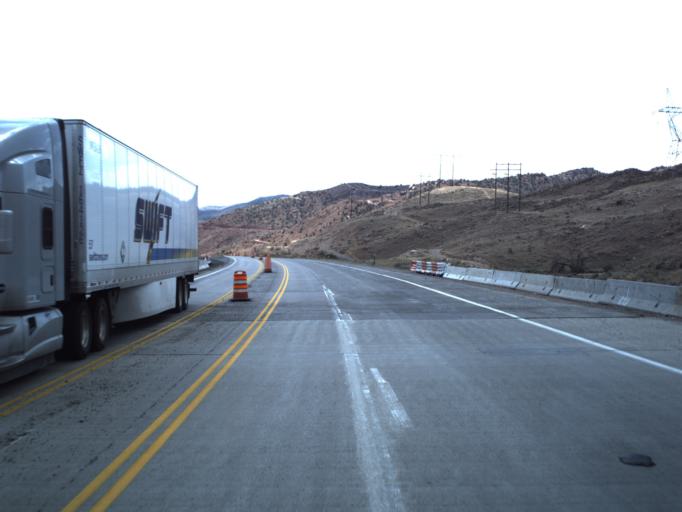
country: US
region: Utah
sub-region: Sevier County
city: Richfield
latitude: 38.7864
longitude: -112.0904
